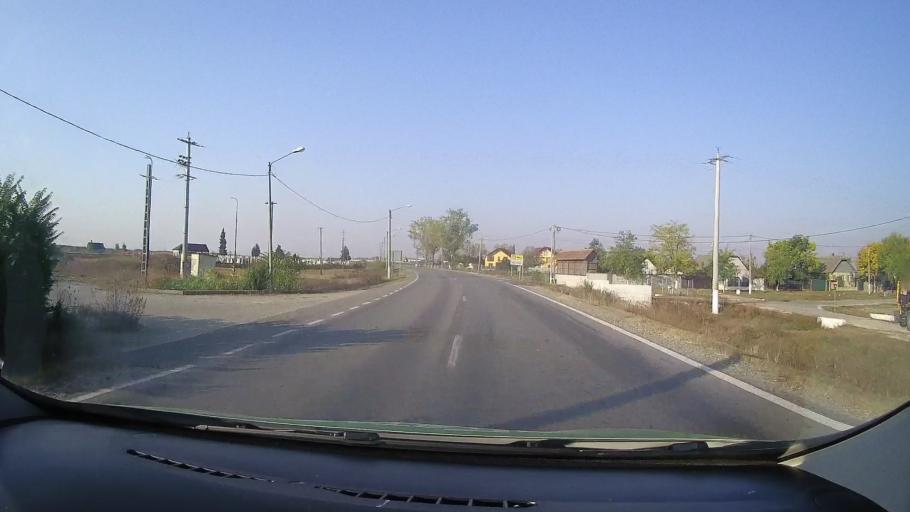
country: RO
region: Arad
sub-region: Comuna Socodor
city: Socodor
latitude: 46.5020
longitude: 21.4453
